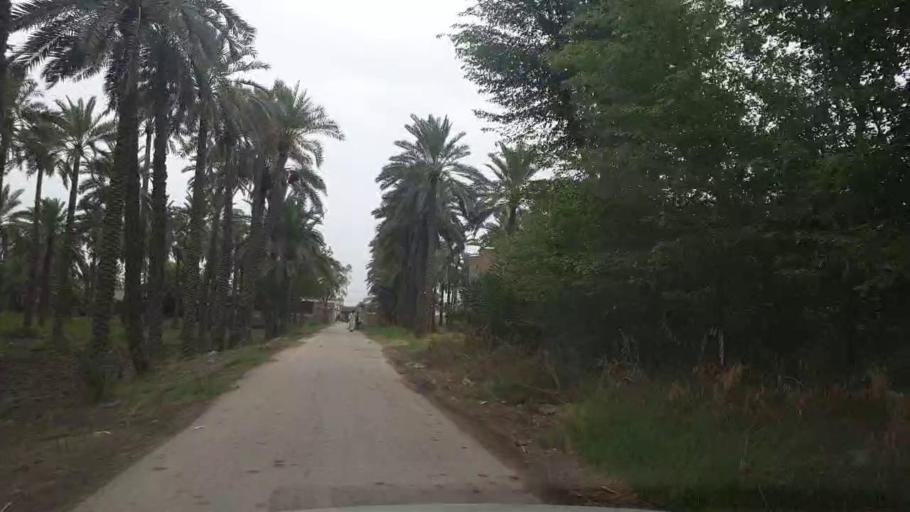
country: PK
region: Sindh
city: Khairpur
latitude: 27.5542
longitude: 68.7507
